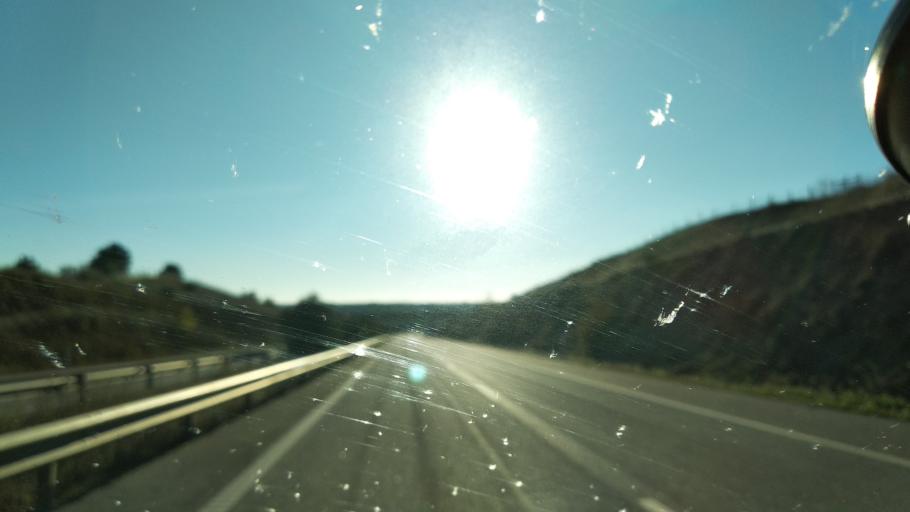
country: PT
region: Santarem
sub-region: Abrantes
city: Alferrarede
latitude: 39.4901
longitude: -8.1173
